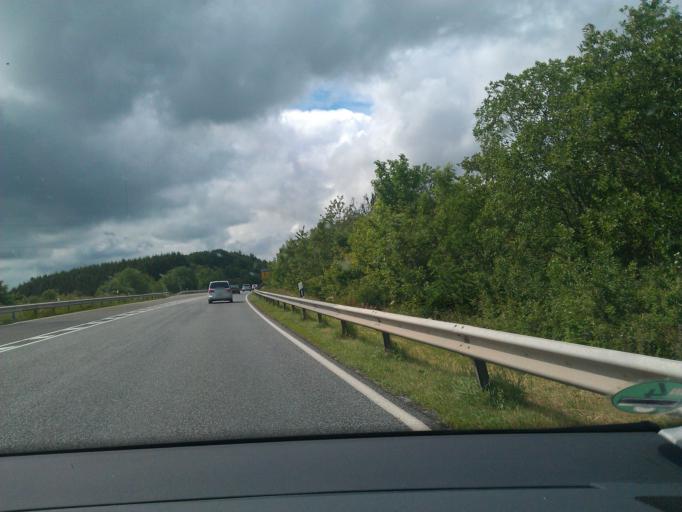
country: DE
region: Rheinland-Pfalz
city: Habscheid
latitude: 50.1993
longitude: 6.2600
